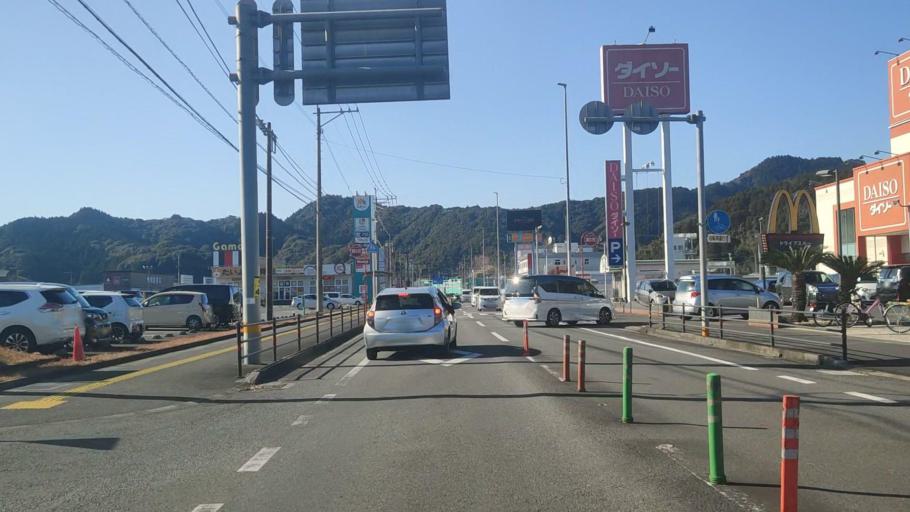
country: JP
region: Oita
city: Saiki
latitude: 32.9611
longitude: 131.8681
